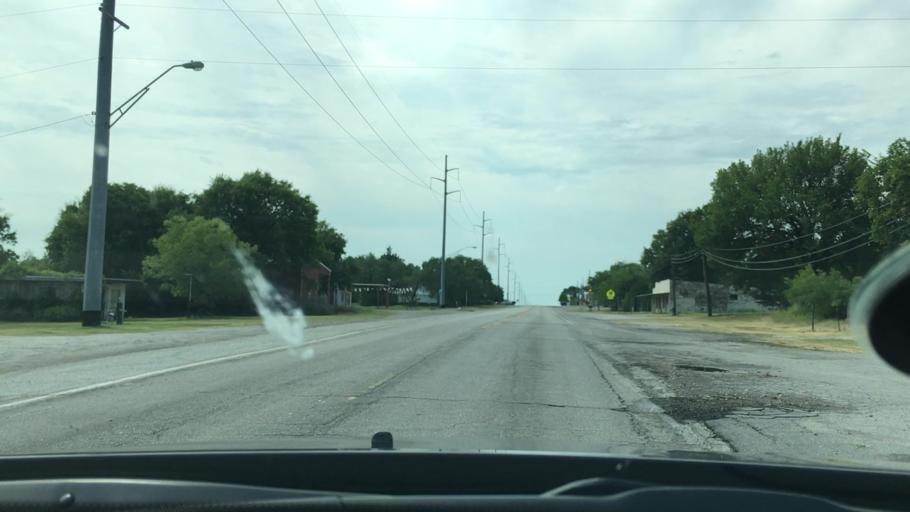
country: US
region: Oklahoma
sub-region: Carter County
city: Ardmore
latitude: 34.3158
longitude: -97.1430
